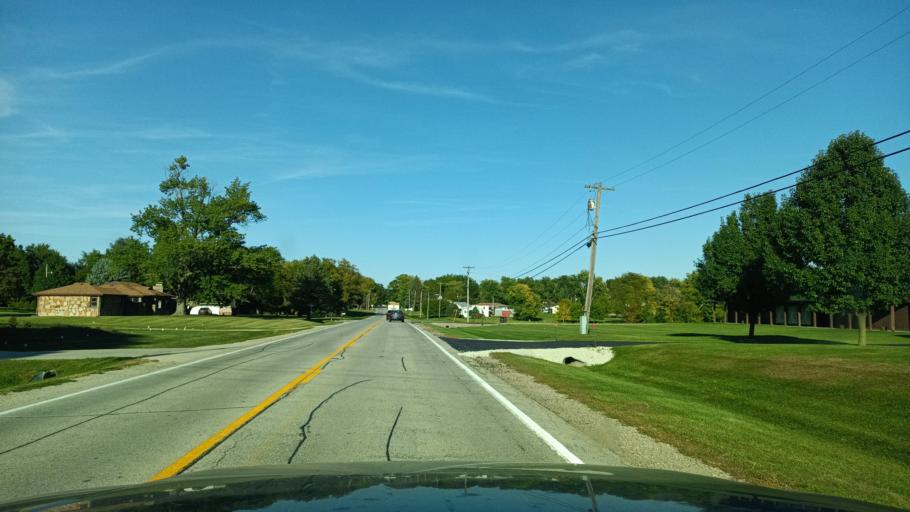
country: US
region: Illinois
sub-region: De Witt County
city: Farmer City
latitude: 40.2357
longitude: -88.6540
